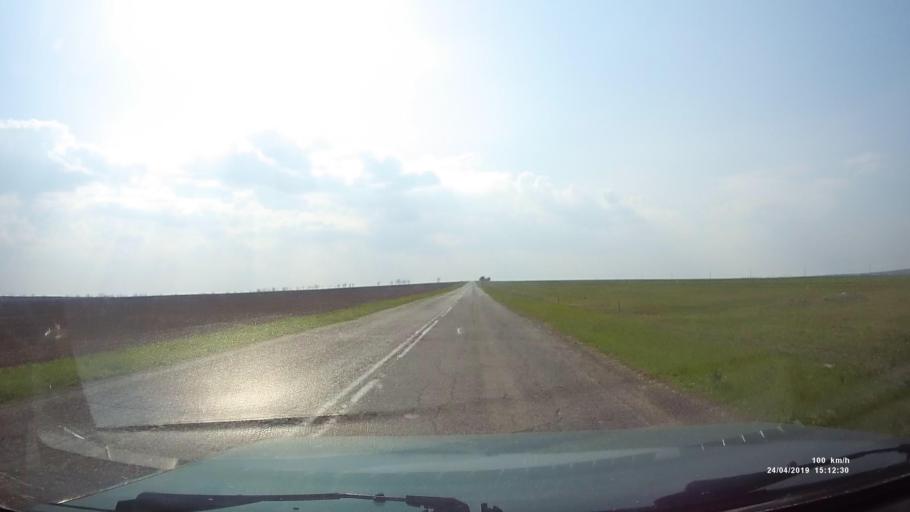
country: RU
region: Rostov
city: Remontnoye
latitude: 46.5464
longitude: 43.2991
